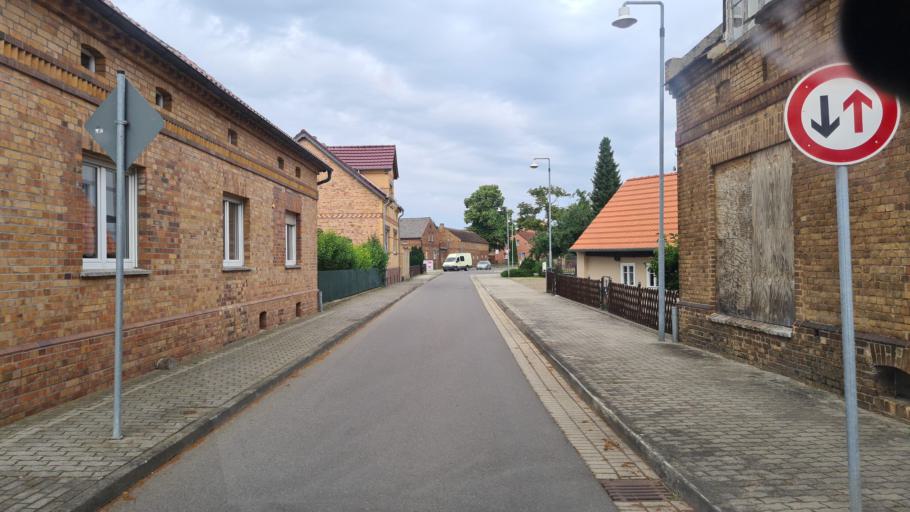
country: DE
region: Brandenburg
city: Grossraschen
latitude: 51.5514
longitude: 14.0596
